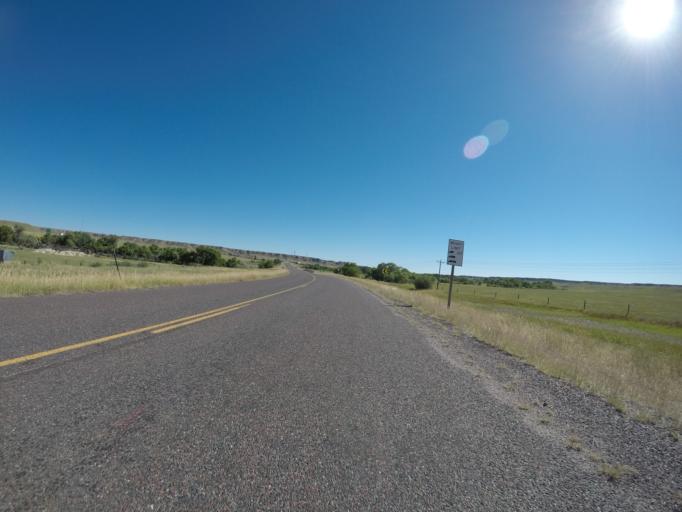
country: US
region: Wyoming
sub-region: Platte County
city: Wheatland
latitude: 41.7474
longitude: -104.8299
